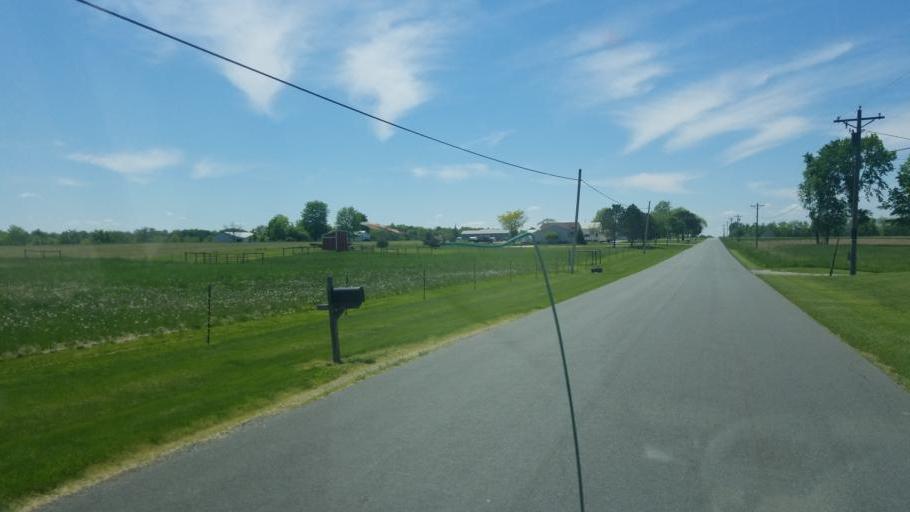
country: US
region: Ohio
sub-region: Huron County
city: Willard
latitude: 41.0834
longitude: -82.7637
